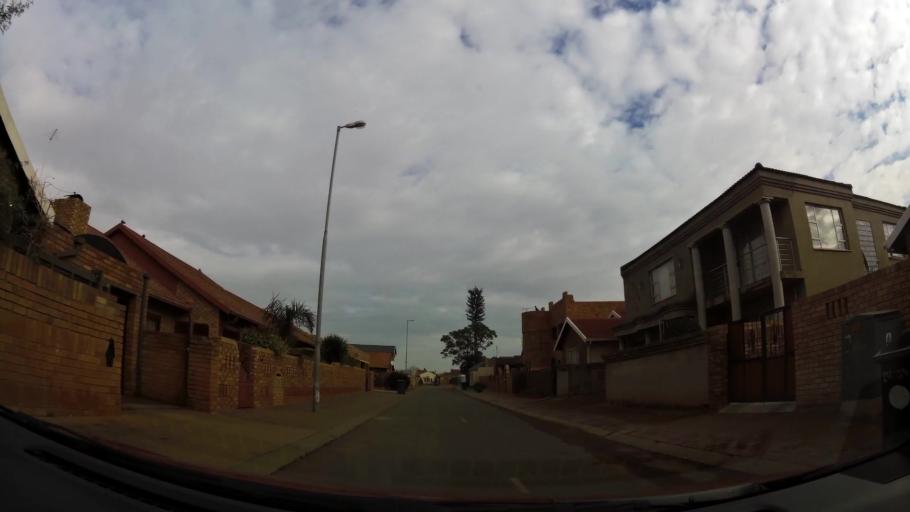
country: ZA
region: Gauteng
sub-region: City of Johannesburg Metropolitan Municipality
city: Soweto
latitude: -26.2692
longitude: 27.8345
